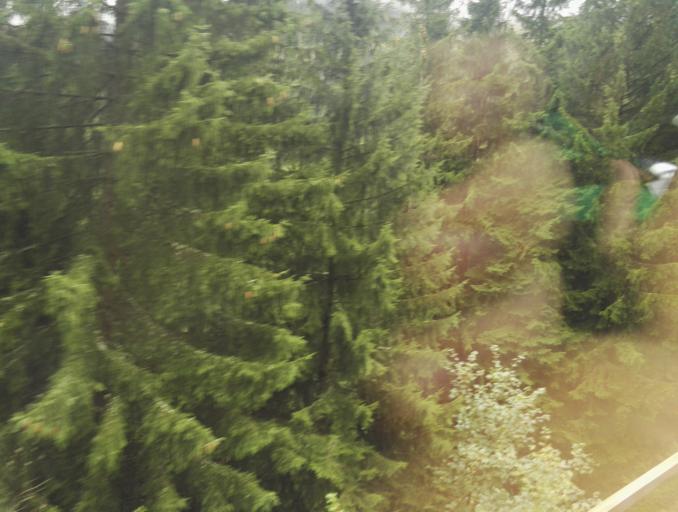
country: AT
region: Styria
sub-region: Politischer Bezirk Leoben
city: Eisenerz
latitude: 47.5273
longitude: 14.9394
